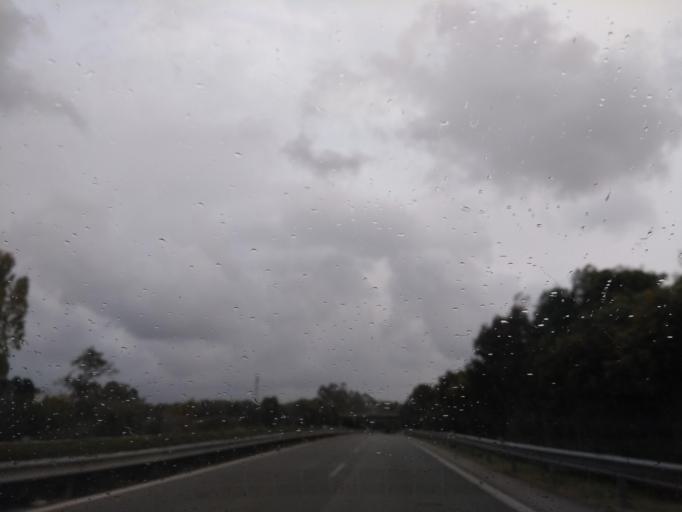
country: IT
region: Sicily
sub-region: Trapani
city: Erice
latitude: 38.0032
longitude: 12.5890
